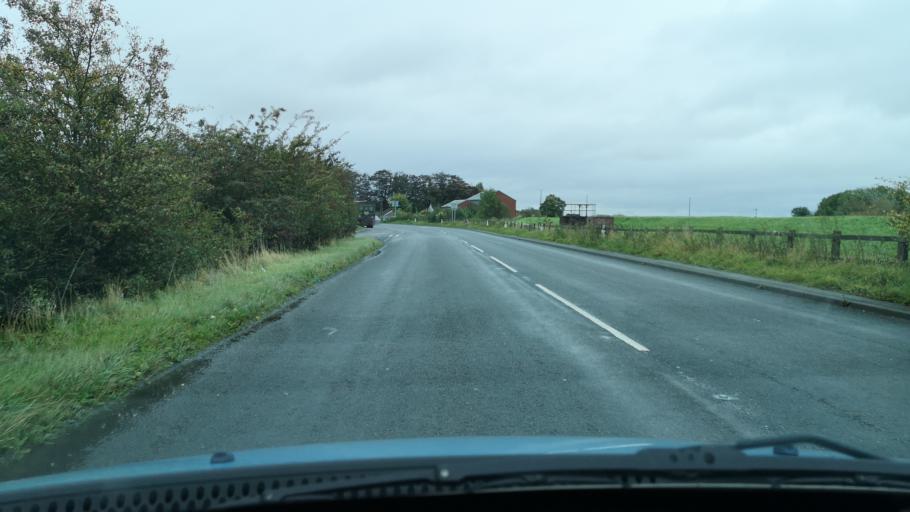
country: GB
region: England
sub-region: Doncaster
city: Hatfield
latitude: 53.6247
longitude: -0.9807
